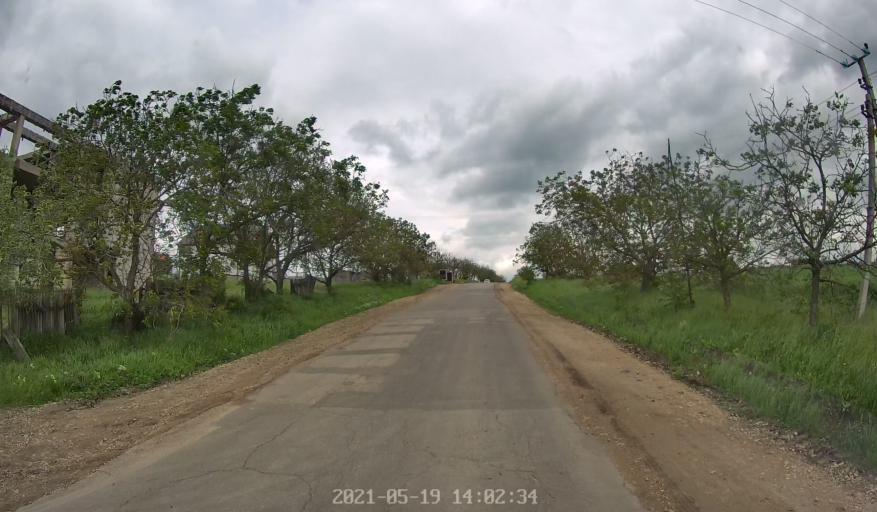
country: MD
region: Chisinau
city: Chisinau
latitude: 47.0354
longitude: 28.9450
